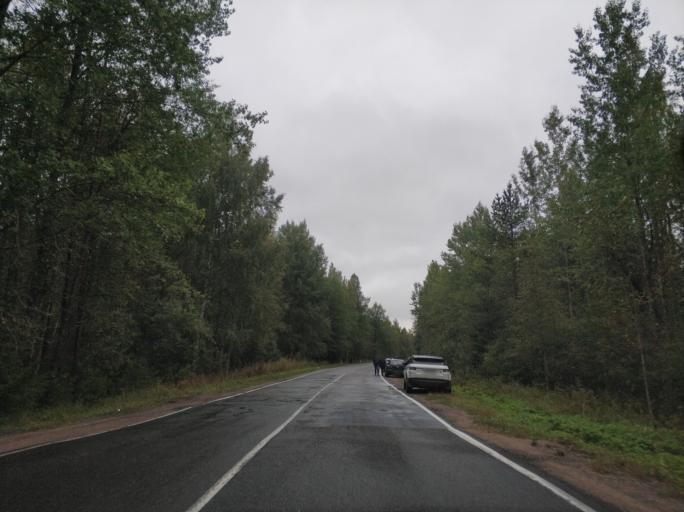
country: RU
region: Leningrad
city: Borisova Griva
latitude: 60.1617
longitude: 30.9223
